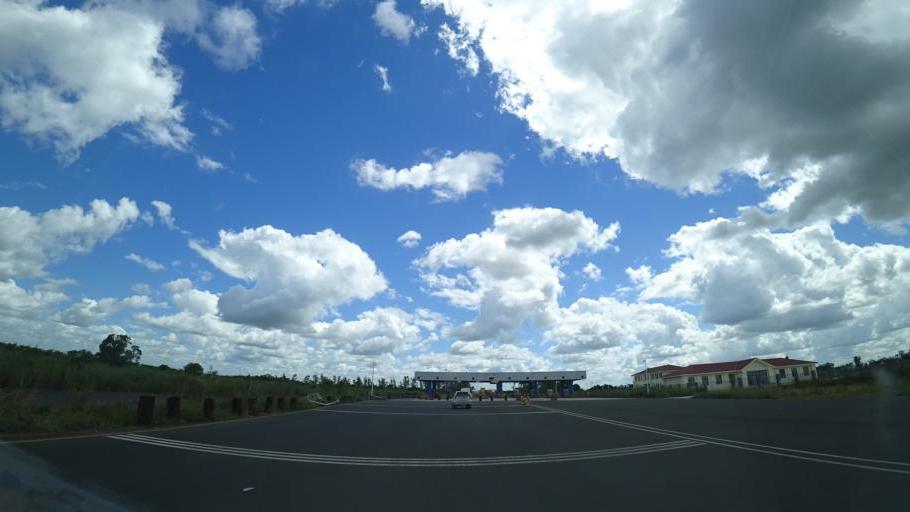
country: MZ
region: Sofala
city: Dondo
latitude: -19.2871
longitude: 34.2273
